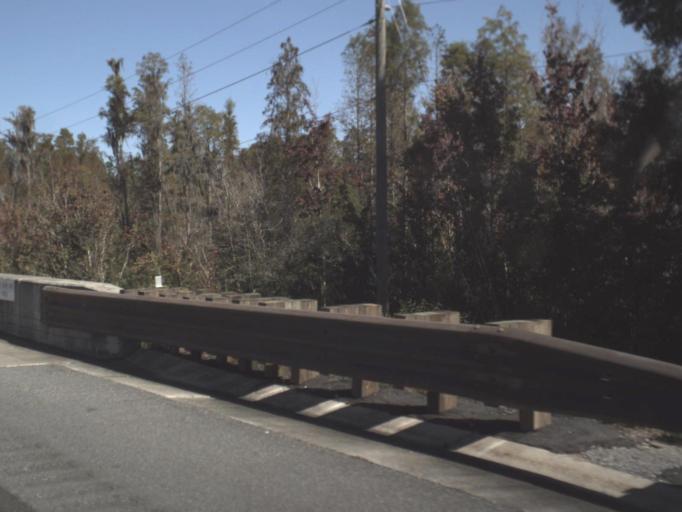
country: US
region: Florida
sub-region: Pasco County
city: Odessa
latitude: 28.2139
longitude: -82.5486
